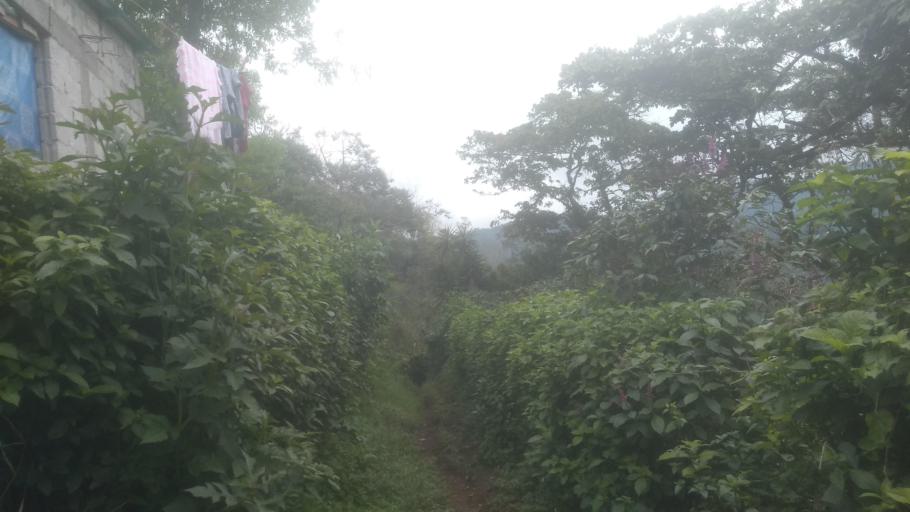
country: MX
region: Veracruz
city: Chocaman
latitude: 18.9895
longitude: -97.0564
